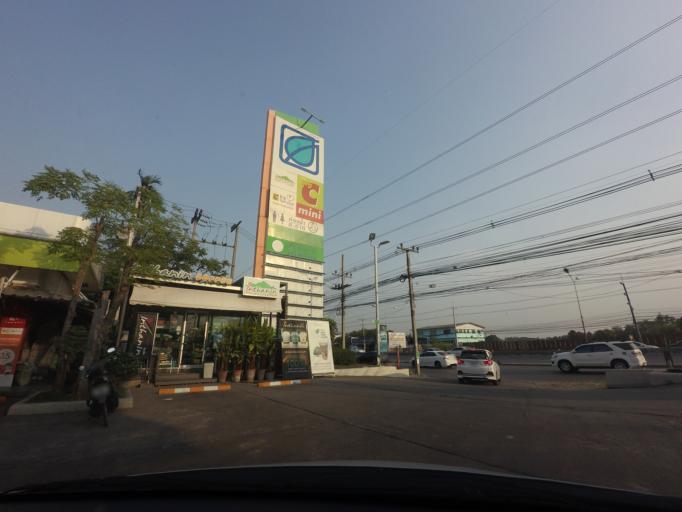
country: TH
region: Nakhon Pathom
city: Salaya
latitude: 13.7864
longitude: 100.2832
